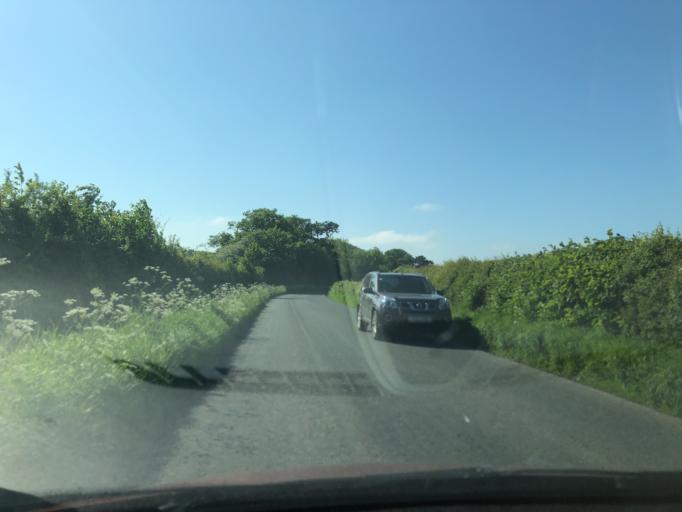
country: GB
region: England
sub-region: North Yorkshire
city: Northallerton
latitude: 54.3215
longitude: -1.3888
